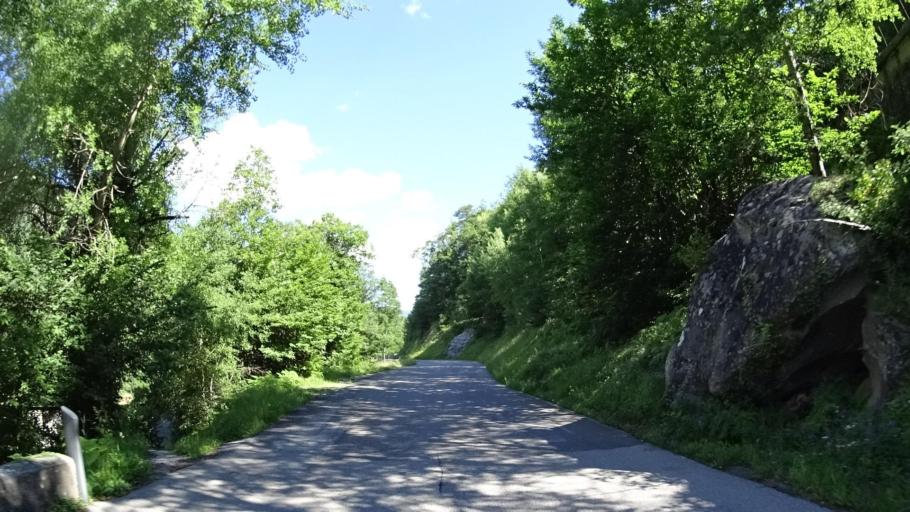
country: FR
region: Provence-Alpes-Cote d'Azur
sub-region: Departement des Alpes-de-Haute-Provence
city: Annot
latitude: 43.9943
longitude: 6.6463
